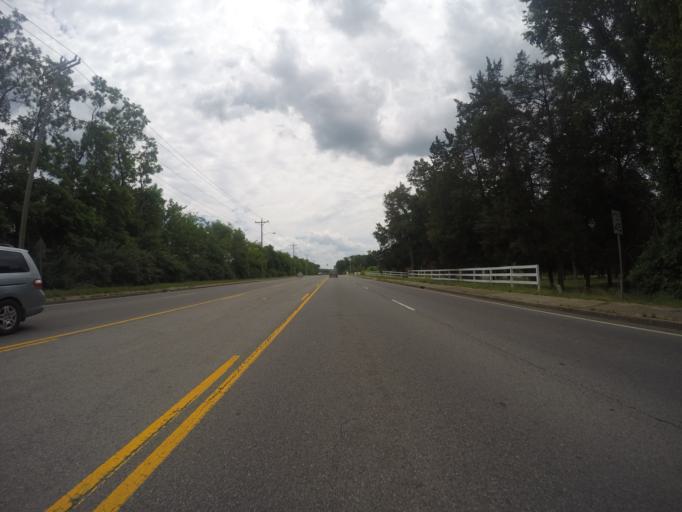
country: US
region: Tennessee
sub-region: Davidson County
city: Lakewood
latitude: 36.2294
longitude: -86.6249
